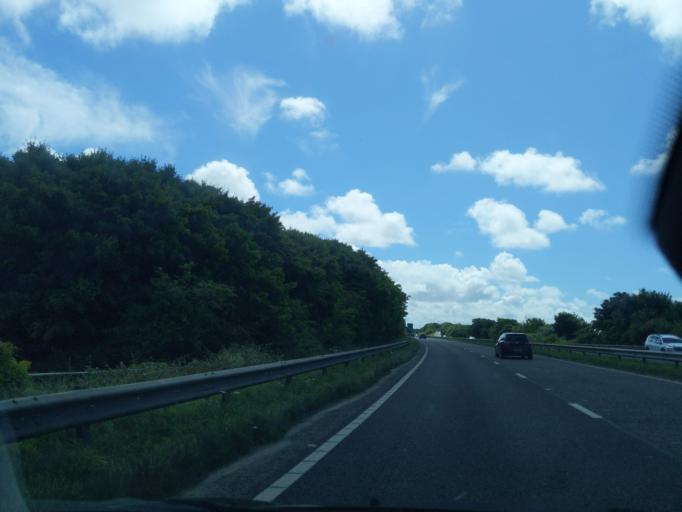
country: GB
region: England
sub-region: Cornwall
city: Redruth
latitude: 50.2479
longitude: -5.2259
